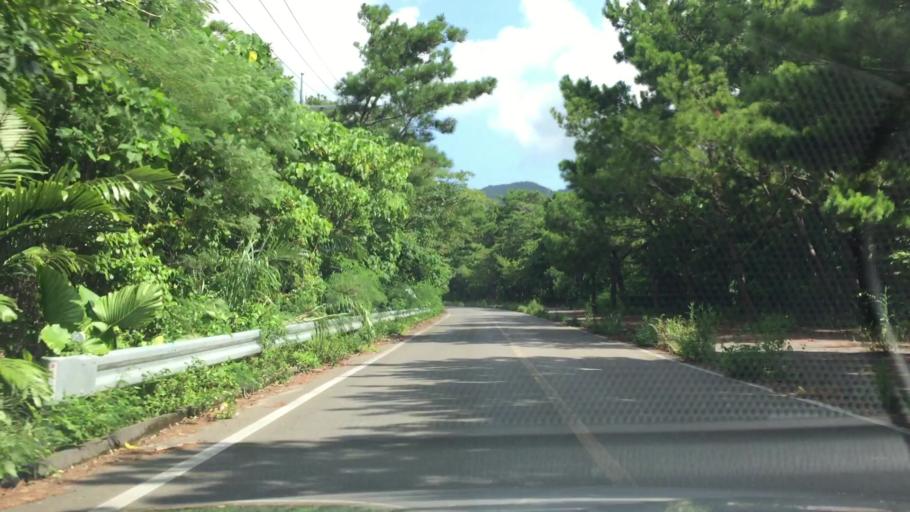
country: JP
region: Okinawa
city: Ishigaki
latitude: 24.4216
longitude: 124.2139
